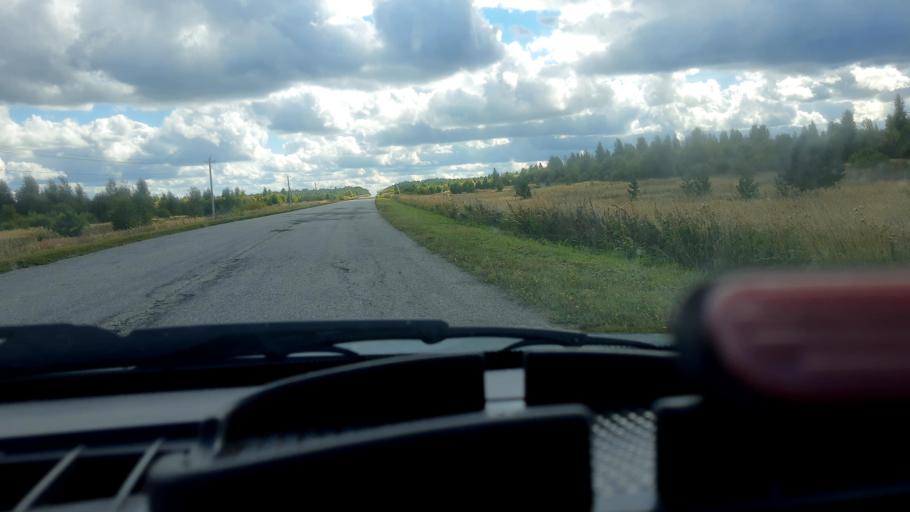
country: RU
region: Mariy-El
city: Kilemary
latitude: 56.9403
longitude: 46.6887
